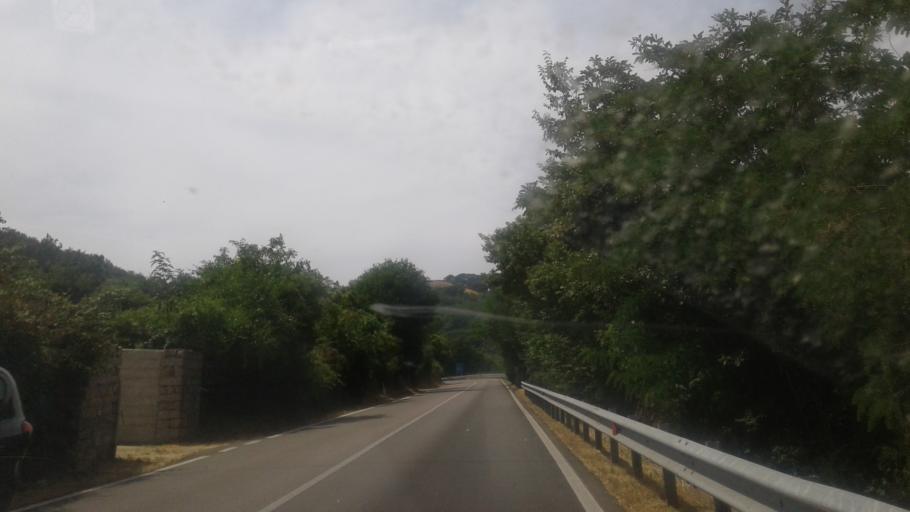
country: IT
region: Sardinia
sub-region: Provincia di Olbia-Tempio
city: Tempio Pausania
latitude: 40.9073
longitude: 9.0902
